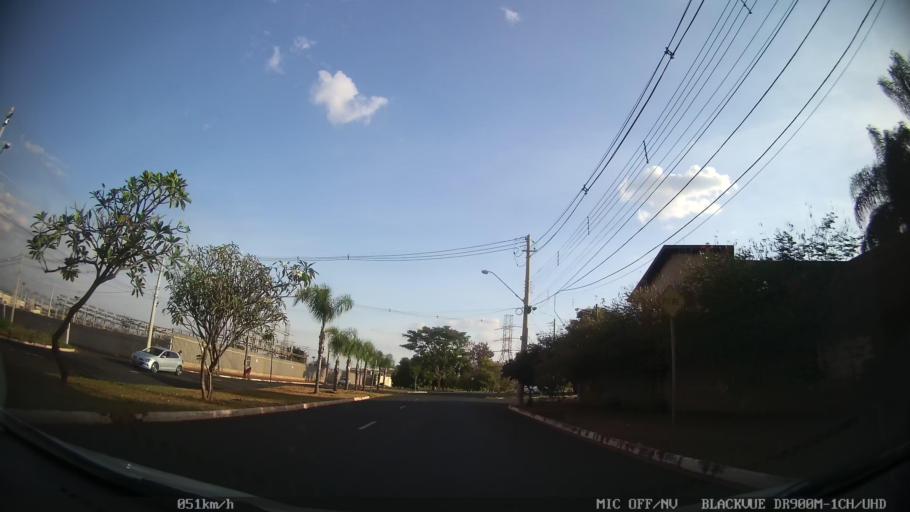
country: BR
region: Sao Paulo
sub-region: Ribeirao Preto
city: Ribeirao Preto
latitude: -21.1598
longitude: -47.8409
